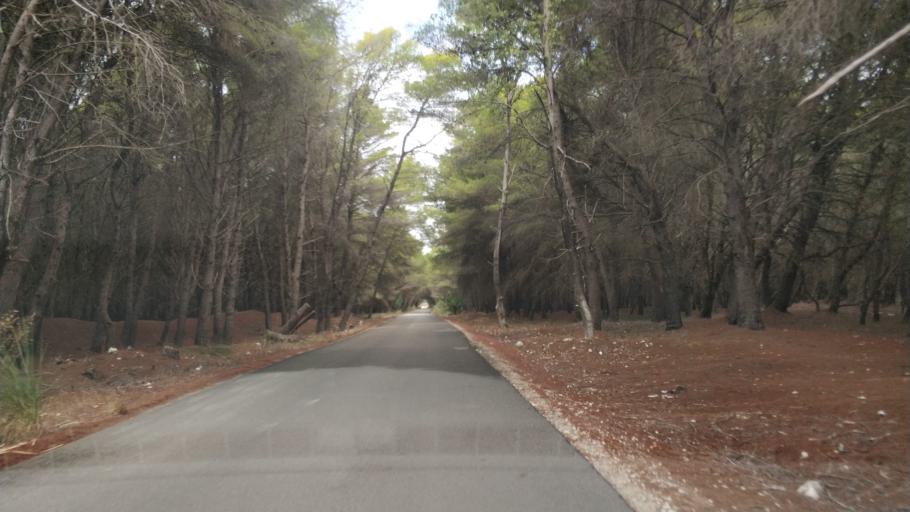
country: AL
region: Vlore
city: Vlore
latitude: 40.4964
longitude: 19.4325
